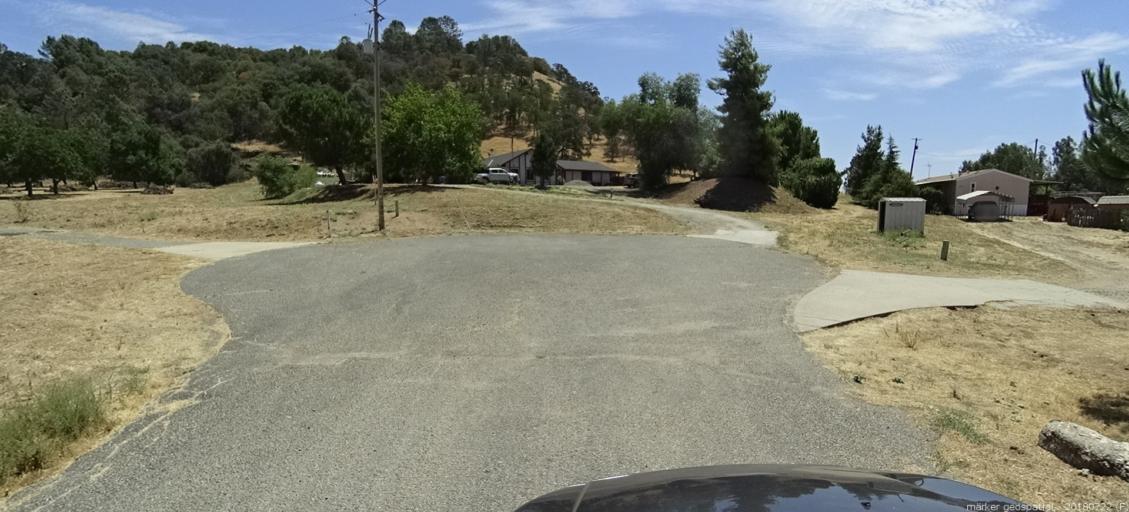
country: US
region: California
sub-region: Madera County
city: Coarsegold
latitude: 37.2616
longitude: -119.7328
